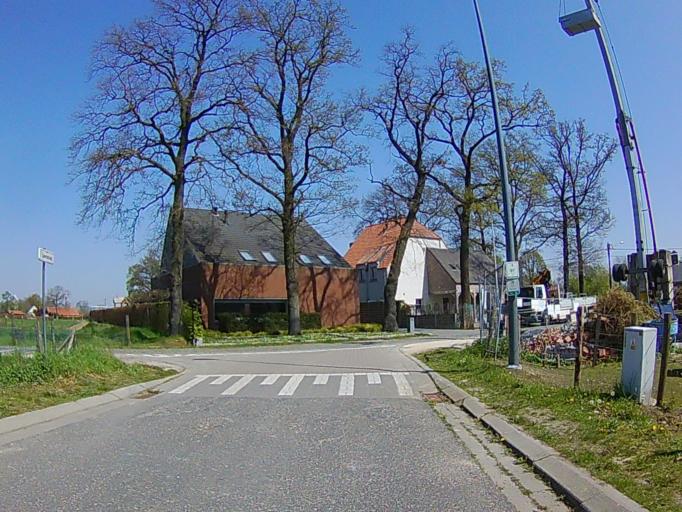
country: BE
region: Flanders
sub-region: Provincie Antwerpen
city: Brecht
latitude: 51.3531
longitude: 4.6640
